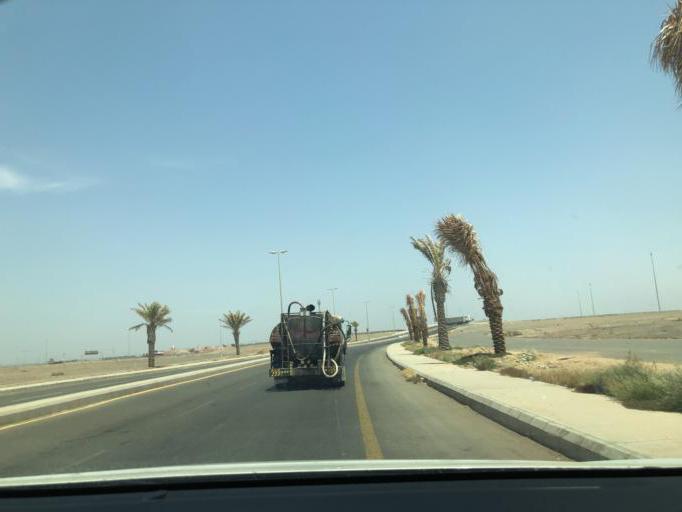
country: SA
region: Makkah
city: Rabigh
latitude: 22.2756
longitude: 39.1217
